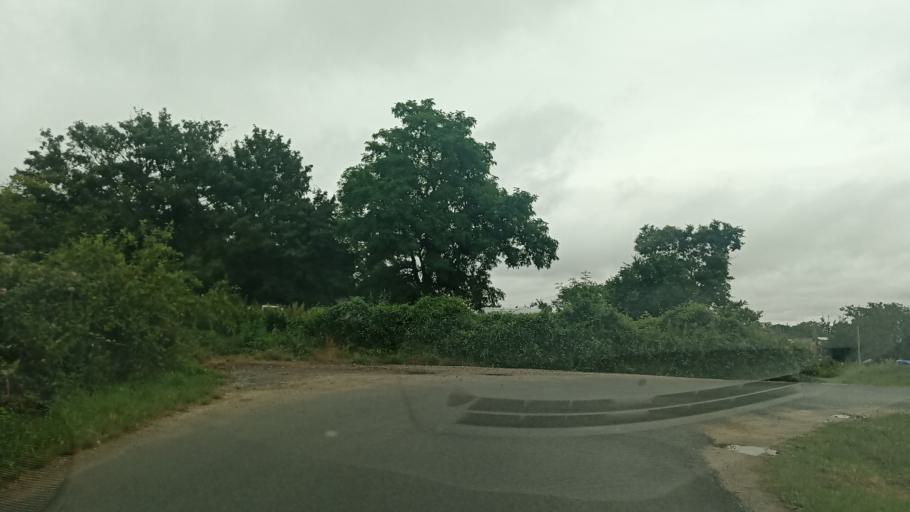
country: FR
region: Poitou-Charentes
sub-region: Departement de la Vienne
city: Vouneuil-sous-Biard
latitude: 46.5942
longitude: 0.2789
